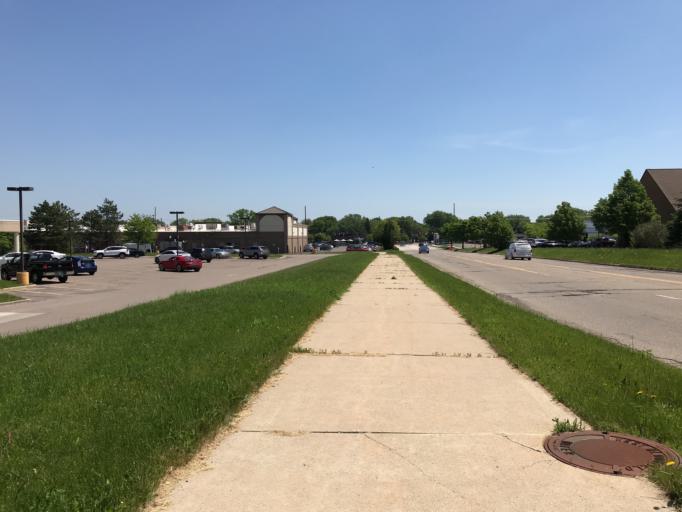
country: US
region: Michigan
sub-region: Oakland County
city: West Bloomfield Township
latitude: 42.5393
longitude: -83.3641
